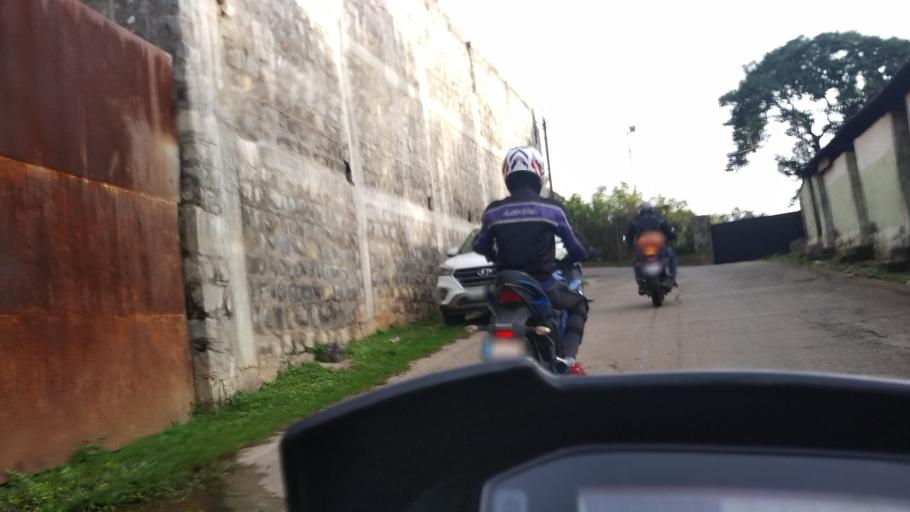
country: IN
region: Tamil Nadu
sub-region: Salem
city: Salem
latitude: 11.7703
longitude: 78.2103
